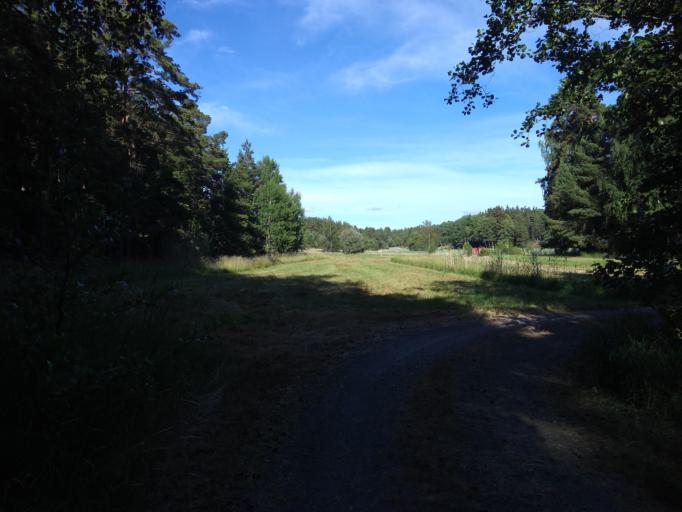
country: FI
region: Varsinais-Suomi
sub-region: Turku
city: Naantali
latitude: 60.4286
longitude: 21.9872
